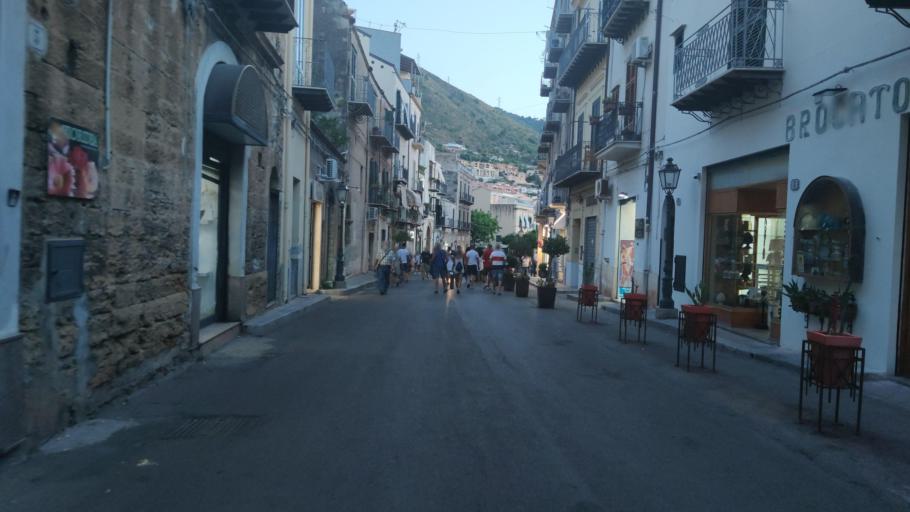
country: IT
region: Sicily
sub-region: Palermo
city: Cefalu
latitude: 38.0366
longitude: 14.0218
